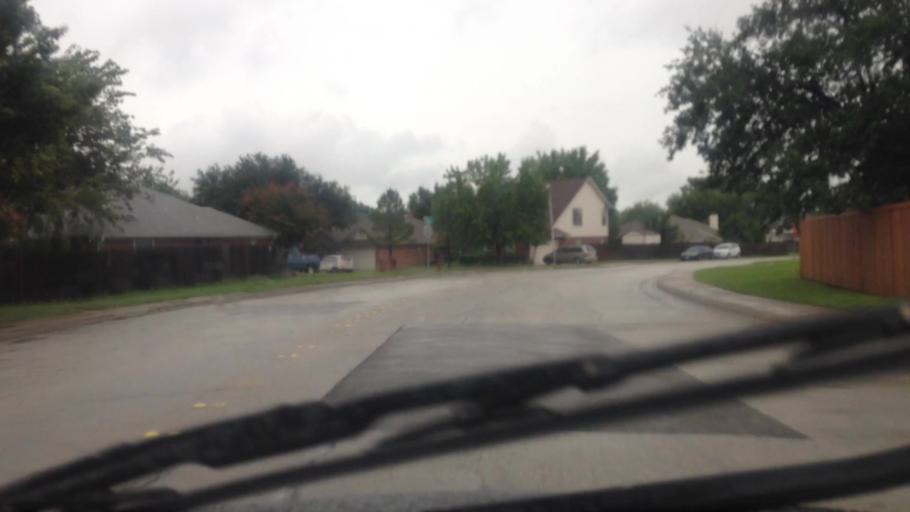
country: US
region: Texas
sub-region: Tarrant County
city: North Richland Hills
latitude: 32.8647
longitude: -97.2187
